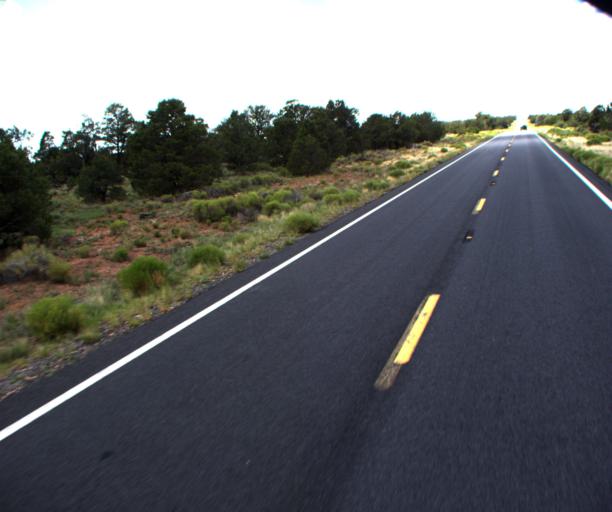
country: US
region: Arizona
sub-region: Coconino County
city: Parks
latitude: 35.5935
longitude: -111.9991
